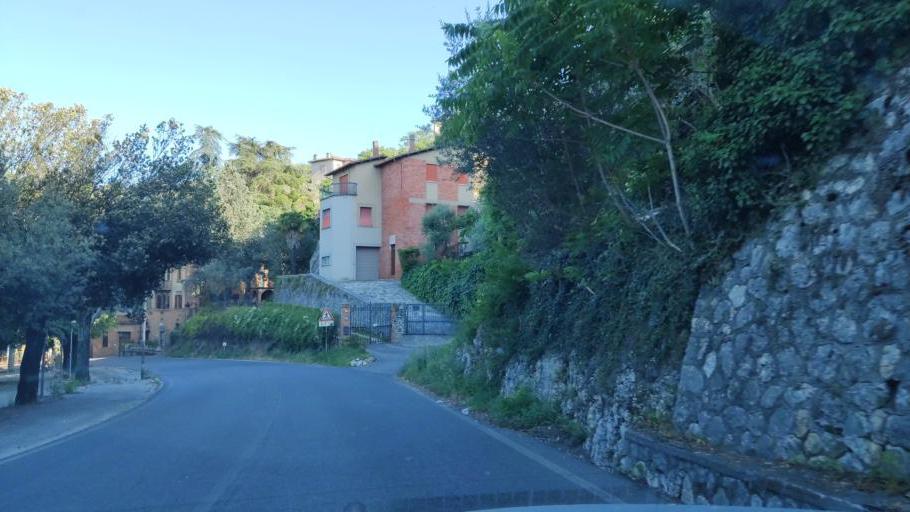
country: IT
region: Umbria
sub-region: Provincia di Terni
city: Narni
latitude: 42.5172
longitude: 12.5224
